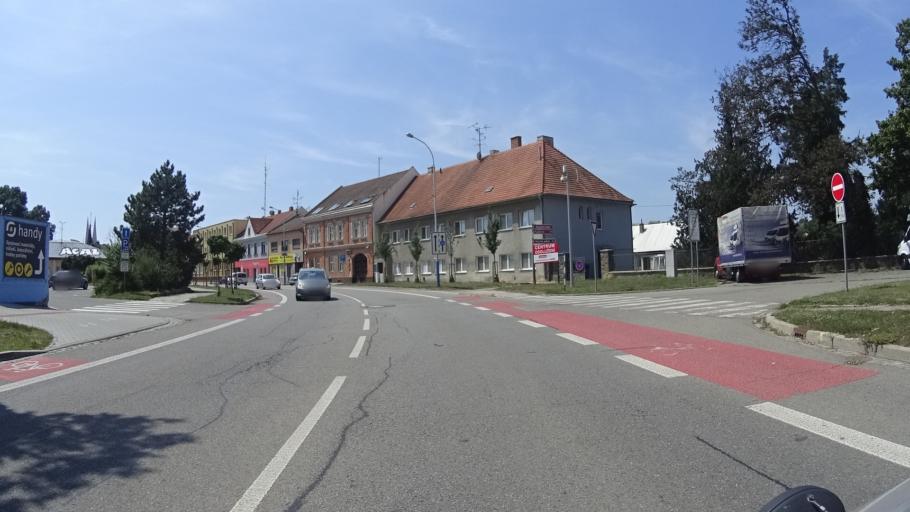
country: CZ
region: South Moravian
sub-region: Okres Breclav
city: Breclav
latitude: 48.7629
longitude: 16.8837
